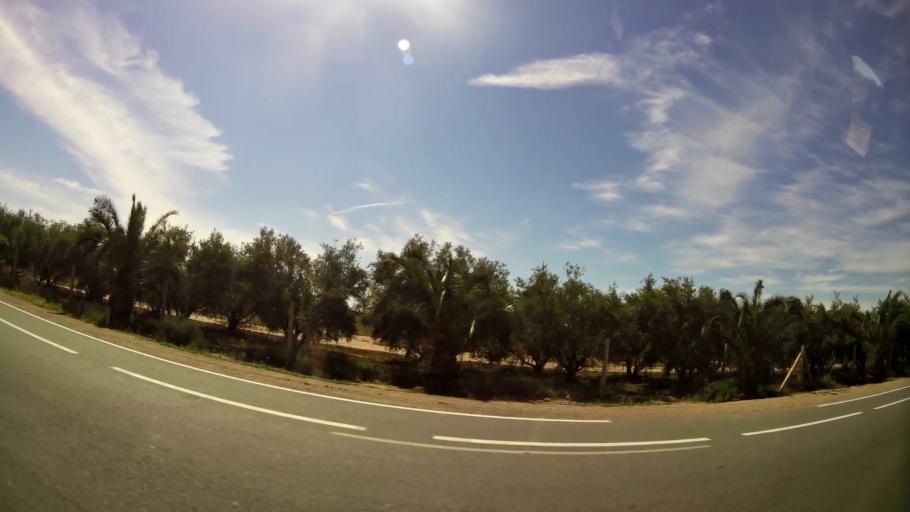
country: MA
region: Marrakech-Tensift-Al Haouz
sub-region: Marrakech
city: Marrakesh
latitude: 31.6600
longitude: -8.1053
